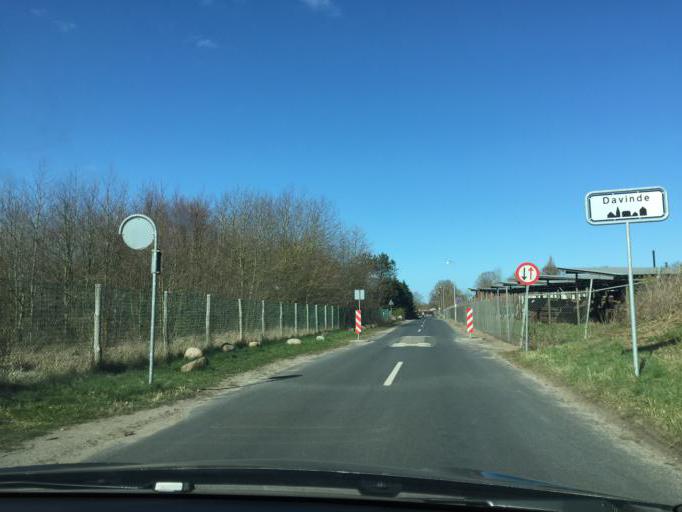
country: DK
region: South Denmark
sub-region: Kerteminde Kommune
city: Langeskov
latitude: 55.3323
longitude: 10.5431
